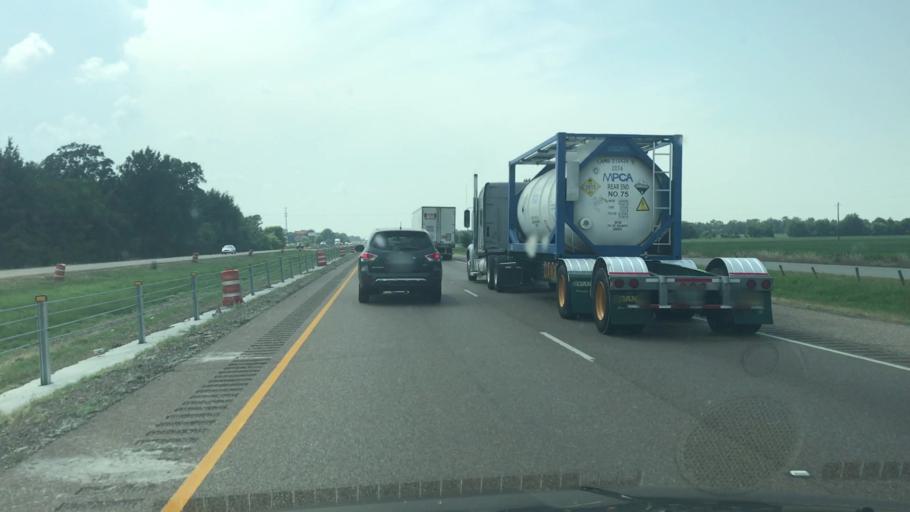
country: US
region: Arkansas
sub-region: Crittenden County
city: West Memphis
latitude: 35.1490
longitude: -90.3437
